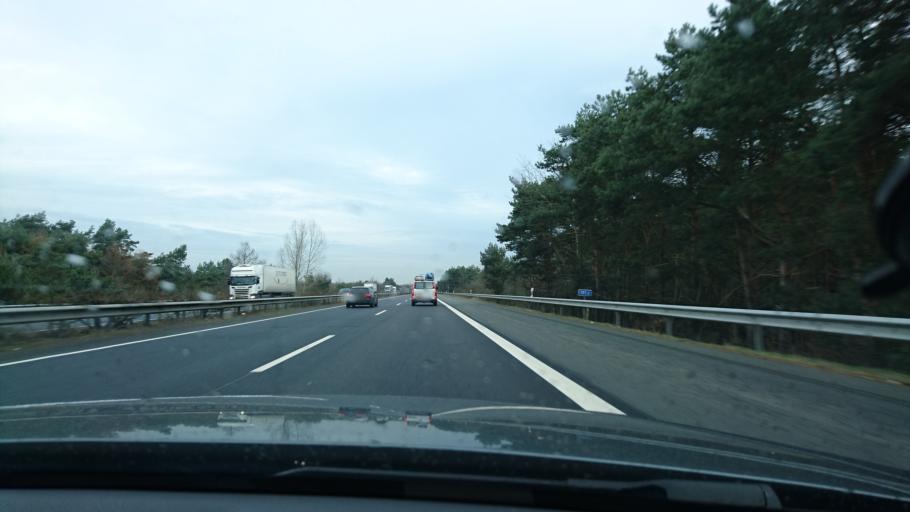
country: DE
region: Lower Saxony
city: Holdorf
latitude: 52.5653
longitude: 8.1121
